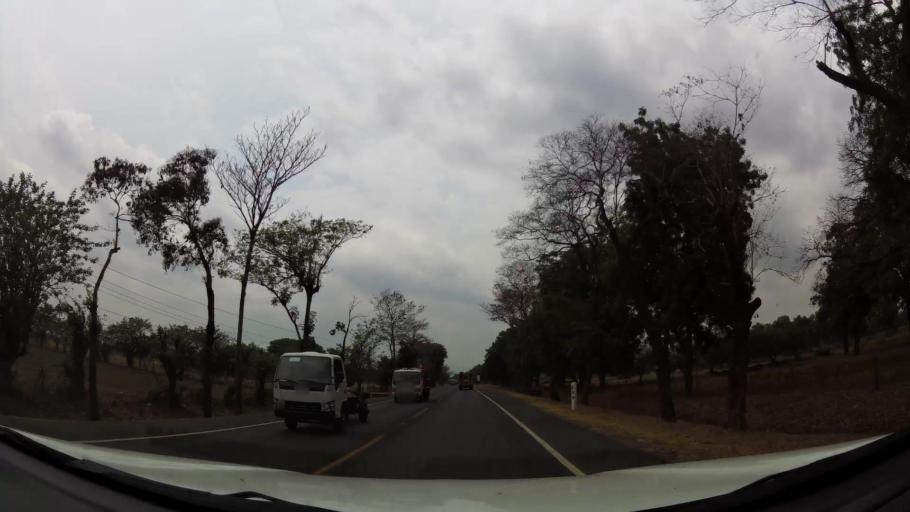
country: NI
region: Leon
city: Telica
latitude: 12.4987
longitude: -86.8600
